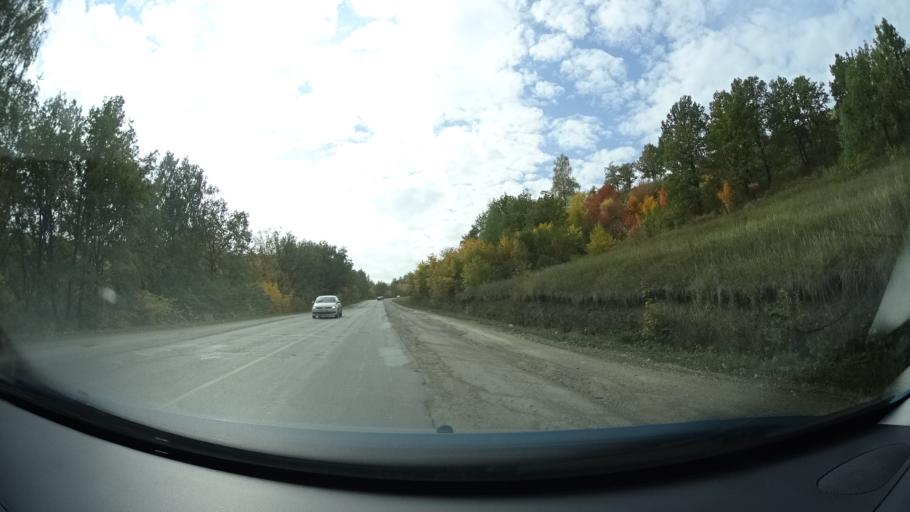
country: RU
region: Tatarstan
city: Urussu
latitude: 54.5496
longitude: 53.5831
